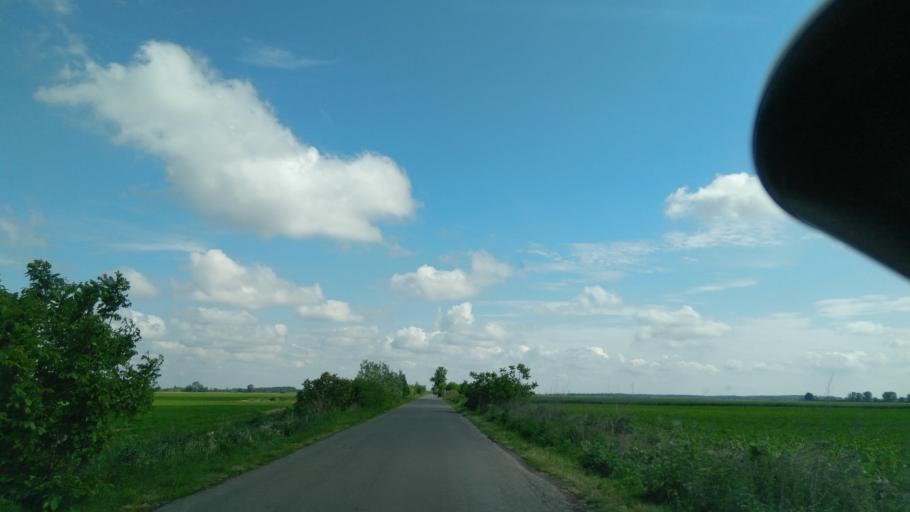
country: HU
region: Bekes
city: Bekes
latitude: 46.8018
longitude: 21.1430
